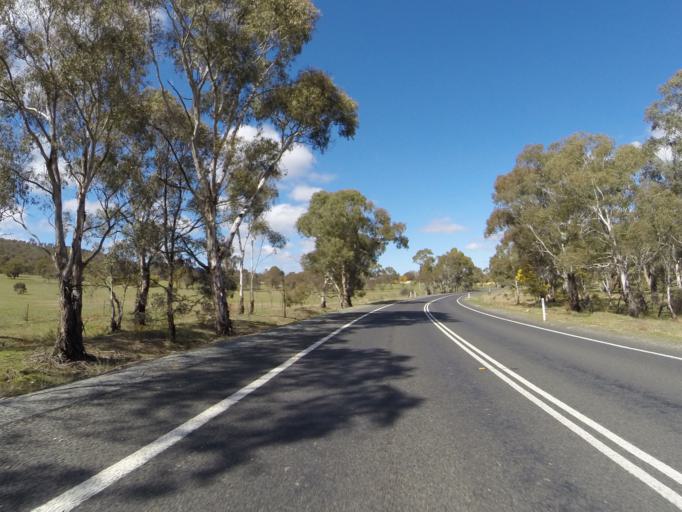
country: AU
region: New South Wales
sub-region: Queanbeyan
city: Queanbeyan
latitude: -35.2394
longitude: 149.2647
